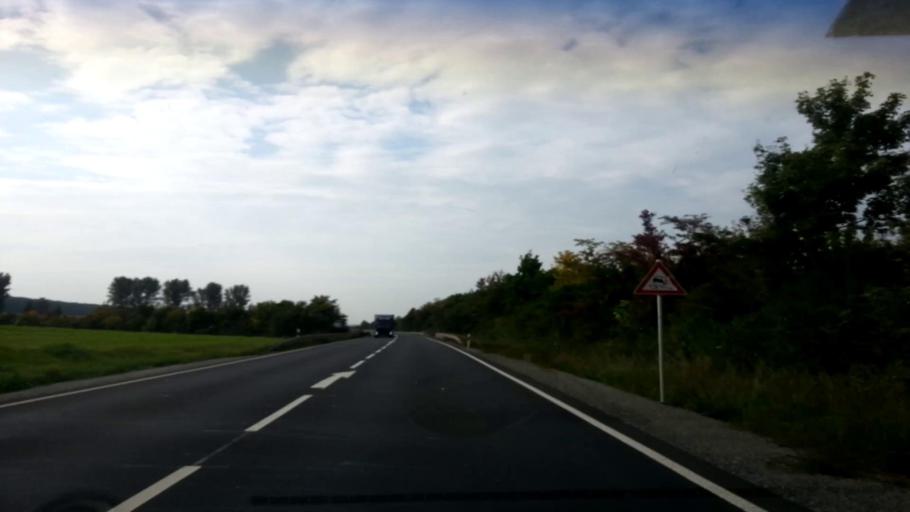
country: DE
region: Bavaria
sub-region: Regierungsbezirk Unterfranken
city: Gerolzhofen
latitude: 49.8930
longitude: 10.3583
